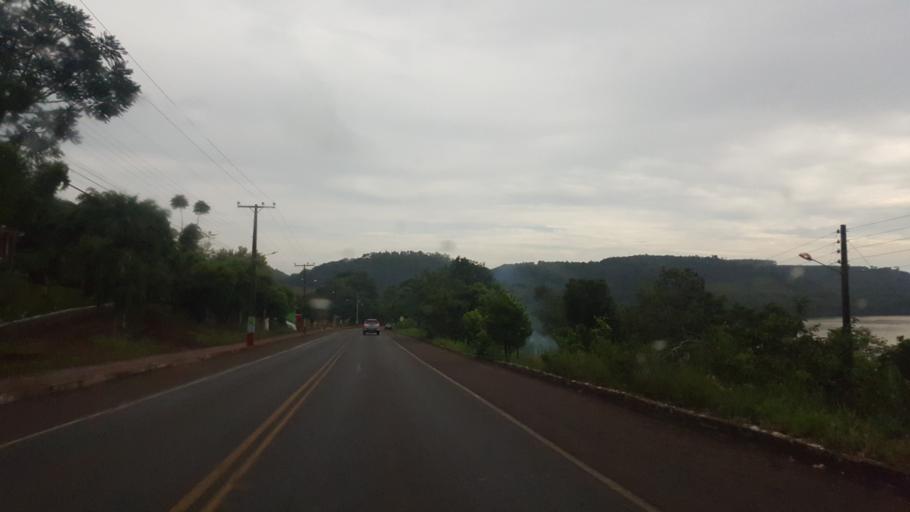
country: BR
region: Rio Grande do Sul
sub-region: Frederico Westphalen
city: Frederico Westphalen
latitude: -27.0948
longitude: -53.3866
